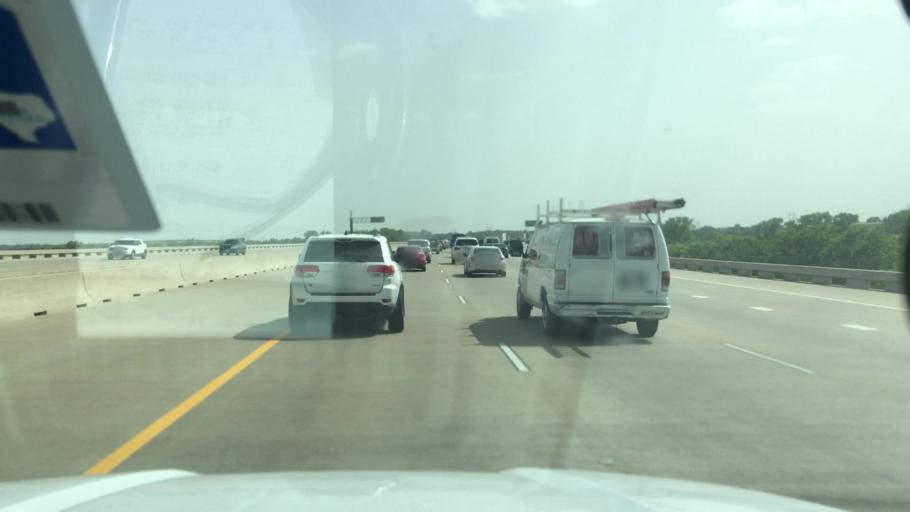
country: US
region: Texas
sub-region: Dallas County
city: Grand Prairie
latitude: 32.7844
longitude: -97.0207
